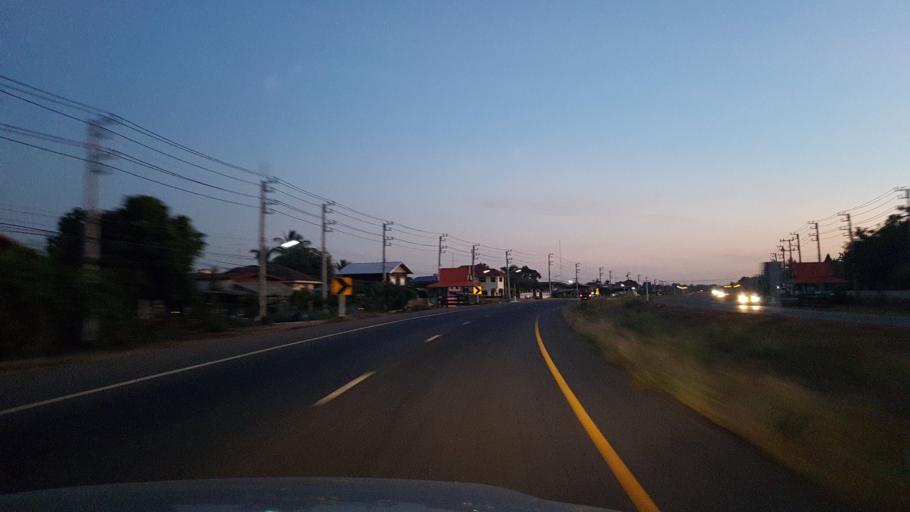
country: TH
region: Chaiyaphum
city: Phu Khiao
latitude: 16.2990
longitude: 102.2097
